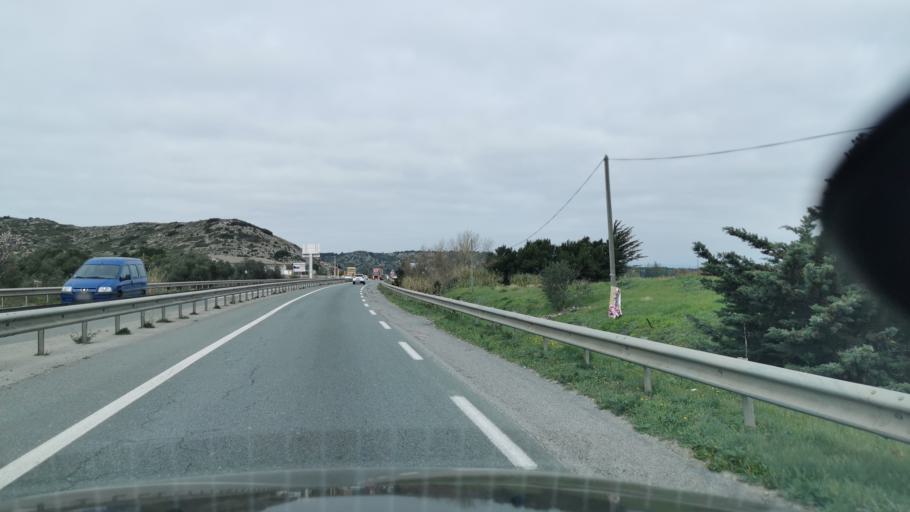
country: FR
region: Languedoc-Roussillon
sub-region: Departement de l'Aude
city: Narbonne
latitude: 43.1721
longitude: 2.9770
